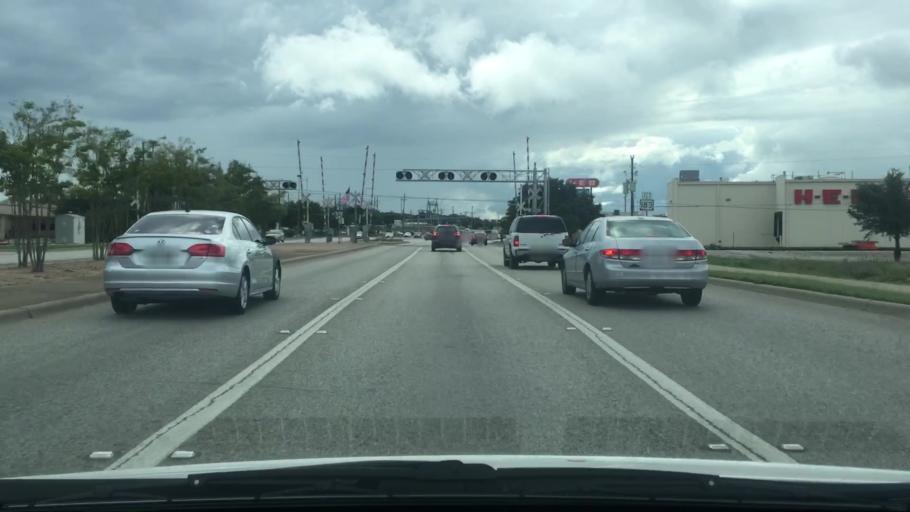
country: US
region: Texas
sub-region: Williamson County
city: Cedar Park
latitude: 30.5220
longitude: -97.8268
